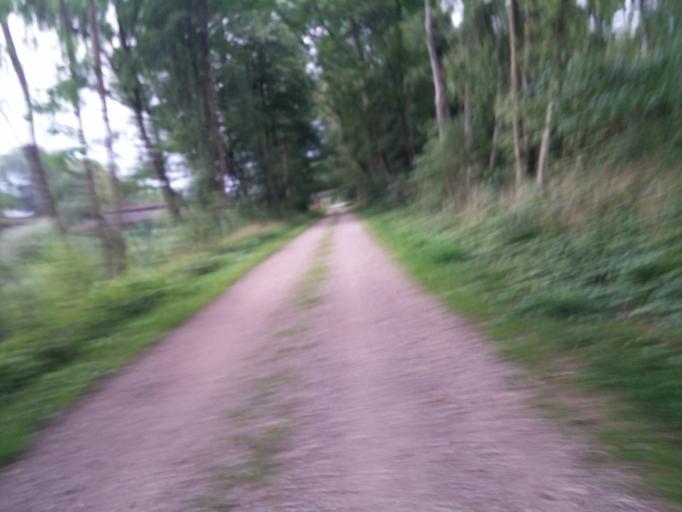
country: DE
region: Bavaria
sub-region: Swabia
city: Buxheim
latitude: 47.9942
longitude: 10.1204
